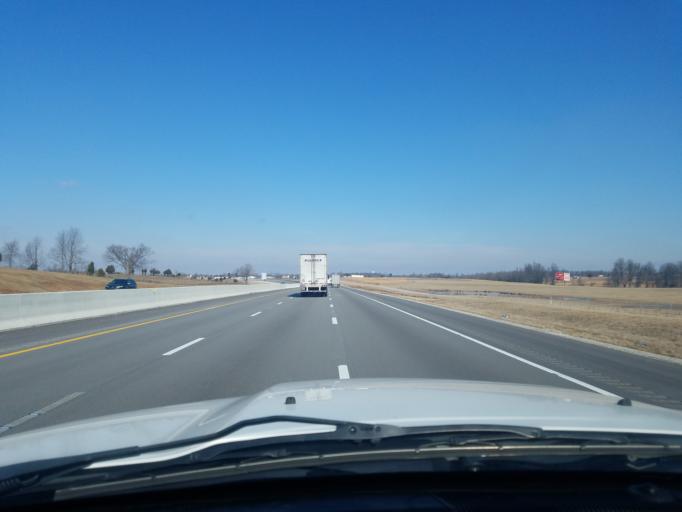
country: US
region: Kentucky
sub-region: Larue County
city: Hodgenville
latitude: 37.4869
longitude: -85.8806
